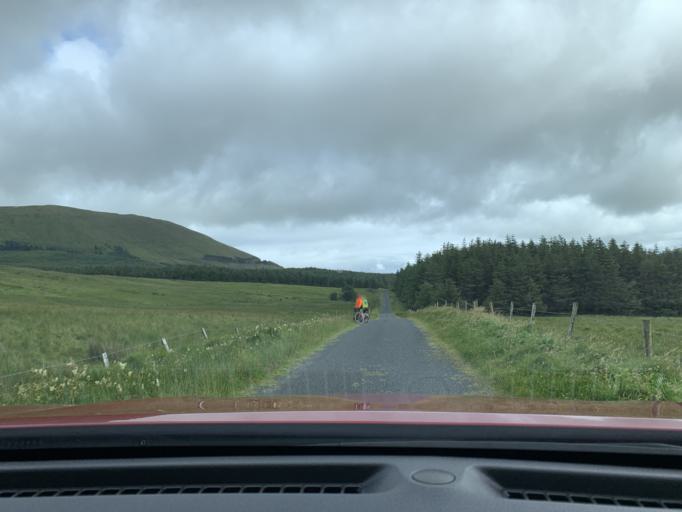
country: IE
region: Connaught
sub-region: Sligo
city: Sligo
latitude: 54.3746
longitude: -8.4150
